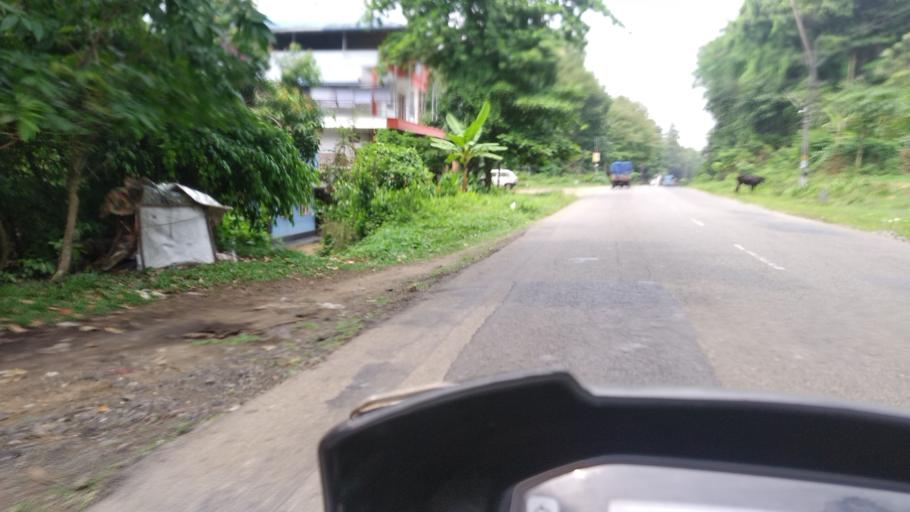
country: IN
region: Kerala
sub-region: Ernakulam
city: Perumpavur
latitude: 10.1005
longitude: 76.5438
